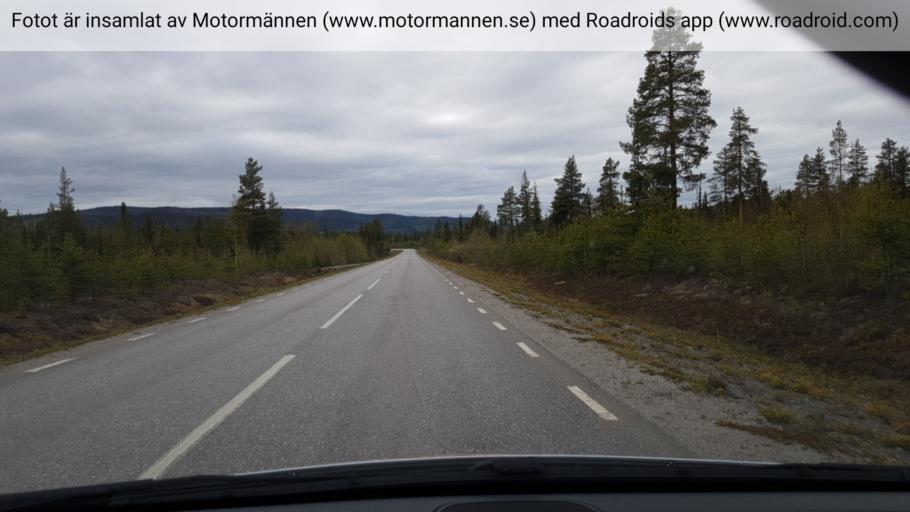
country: SE
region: Vaesterbotten
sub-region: Sorsele Kommun
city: Sorsele
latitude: 65.5442
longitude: 17.4357
